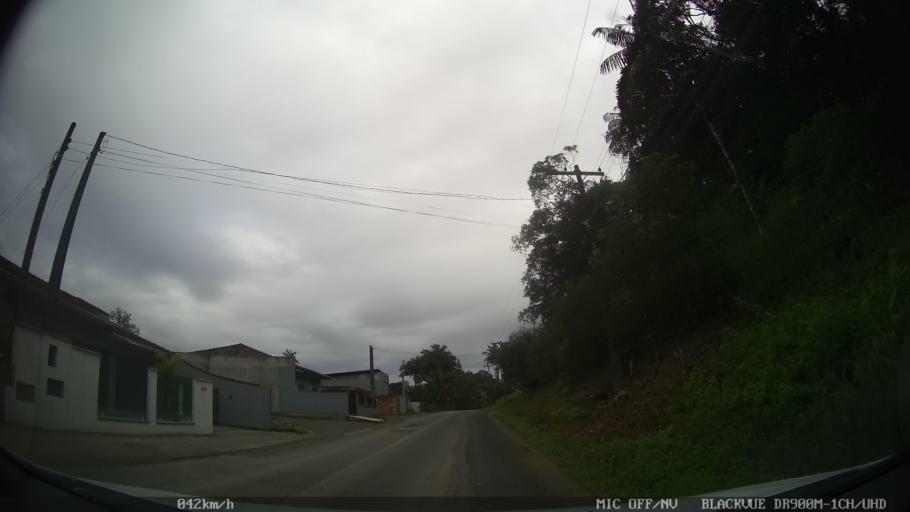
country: BR
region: Santa Catarina
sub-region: Joinville
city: Joinville
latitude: -26.2826
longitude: -48.9246
